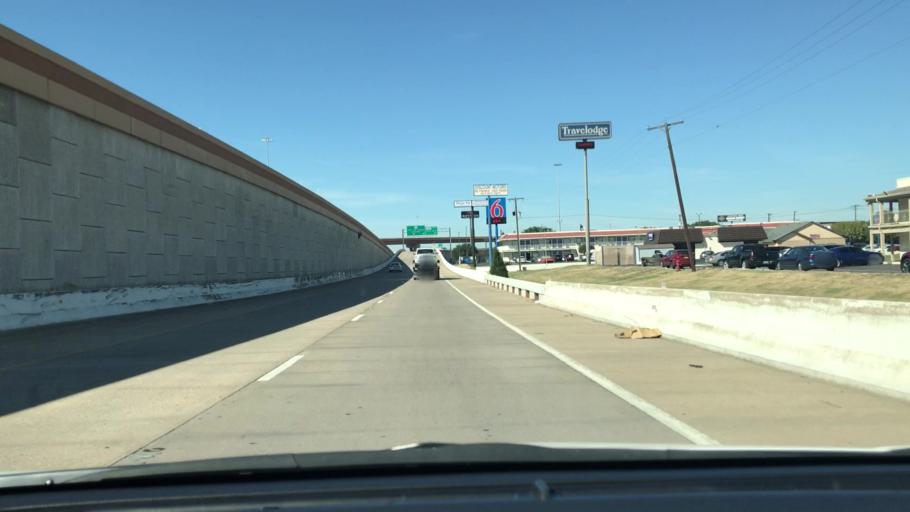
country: US
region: Texas
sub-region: Tarrant County
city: North Richland Hills
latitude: 32.8332
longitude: -97.2087
